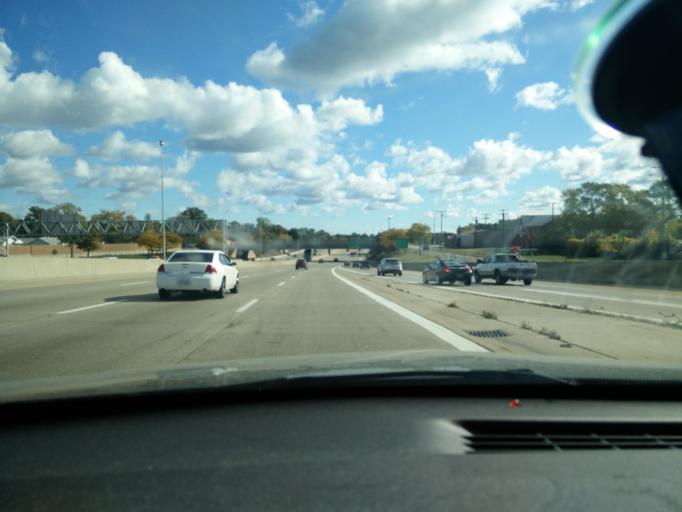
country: US
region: Michigan
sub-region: Oakland County
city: Madison Heights
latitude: 42.4768
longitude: -83.1078
